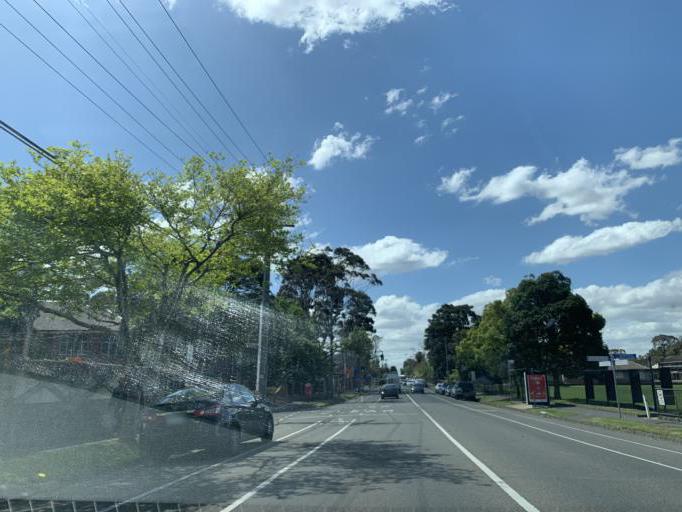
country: AU
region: Victoria
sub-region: Bayside
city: North Brighton
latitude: -37.9100
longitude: 144.9921
